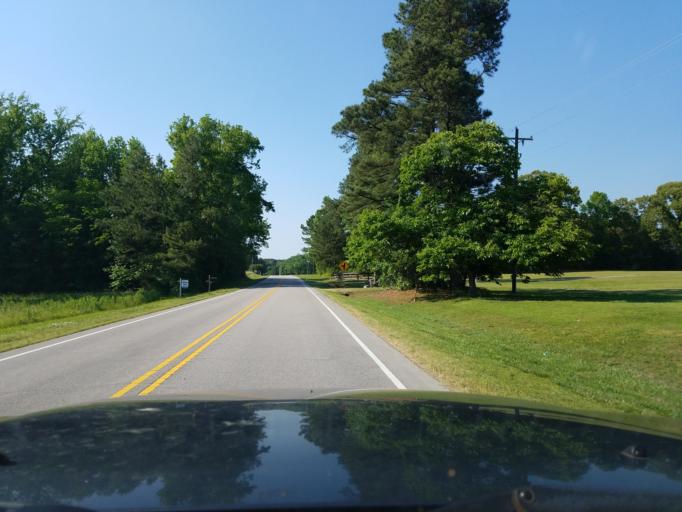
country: US
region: North Carolina
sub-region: Vance County
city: Henderson
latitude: 36.3998
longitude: -78.3684
